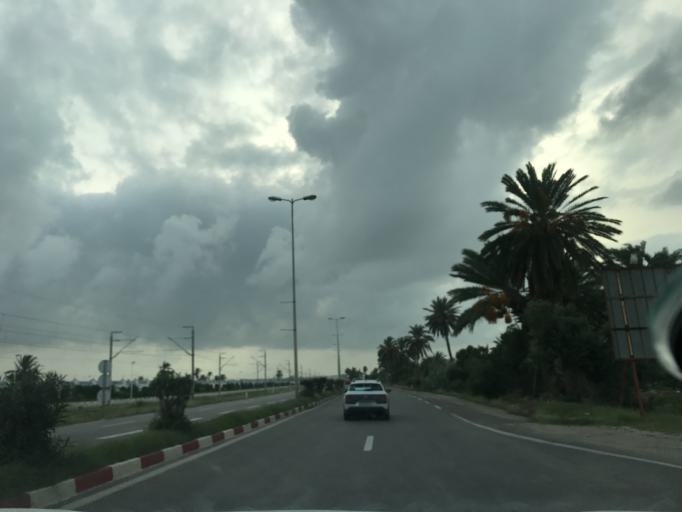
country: TN
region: Al Munastir
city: Sahline
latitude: 35.7592
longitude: 10.7411
